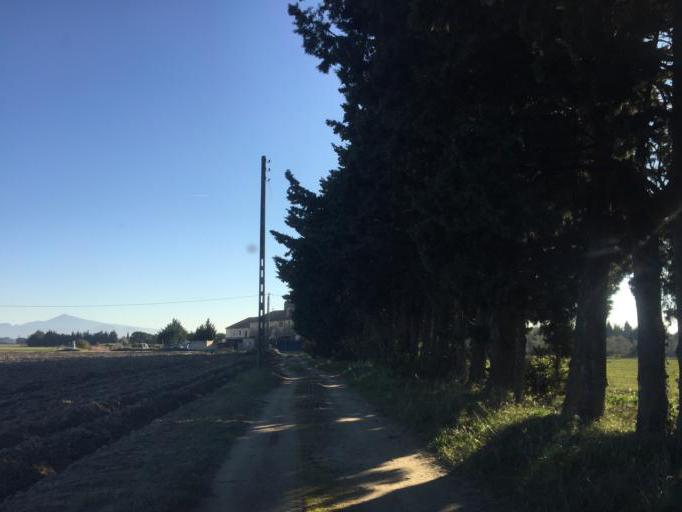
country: FR
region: Provence-Alpes-Cote d'Azur
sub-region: Departement du Vaucluse
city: Orange
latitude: 44.1554
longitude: 4.8108
